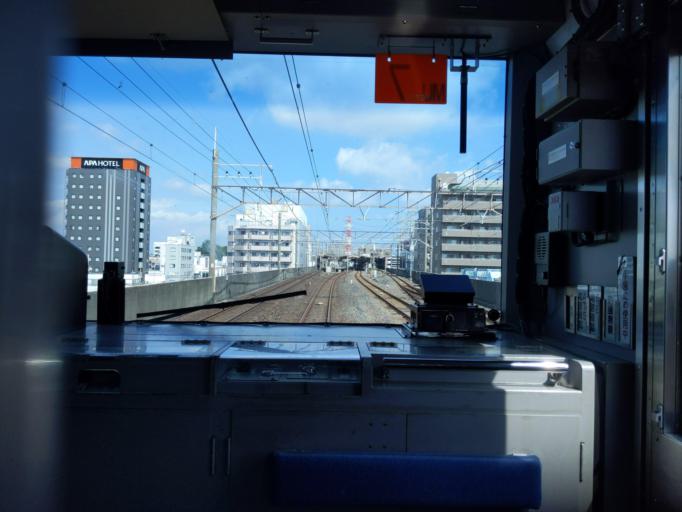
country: JP
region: Chiba
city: Funabashi
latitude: 35.7047
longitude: 139.9578
